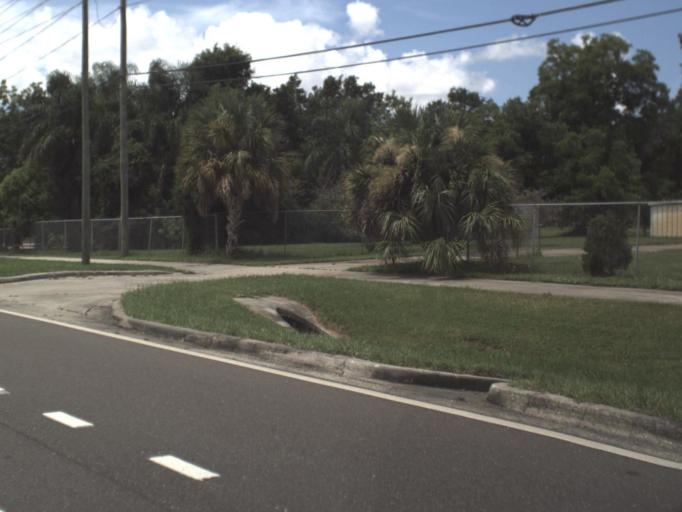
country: US
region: Florida
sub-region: Pinellas County
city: Safety Harbor
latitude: 27.9917
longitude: -82.7091
